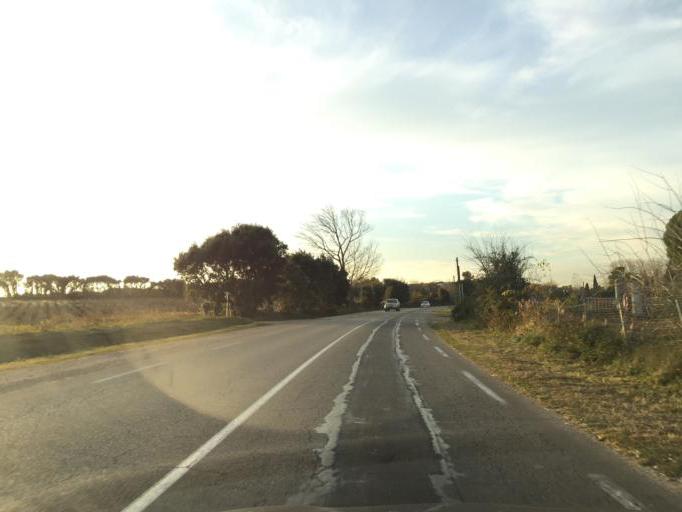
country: FR
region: Provence-Alpes-Cote d'Azur
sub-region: Departement du Vaucluse
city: Courthezon
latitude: 44.1173
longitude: 4.8562
